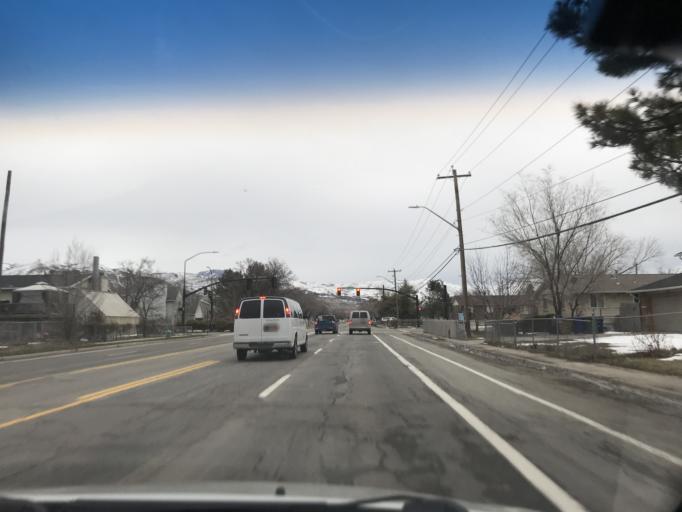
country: US
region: Utah
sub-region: Salt Lake County
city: Salt Lake City
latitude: 40.7847
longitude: -111.9466
